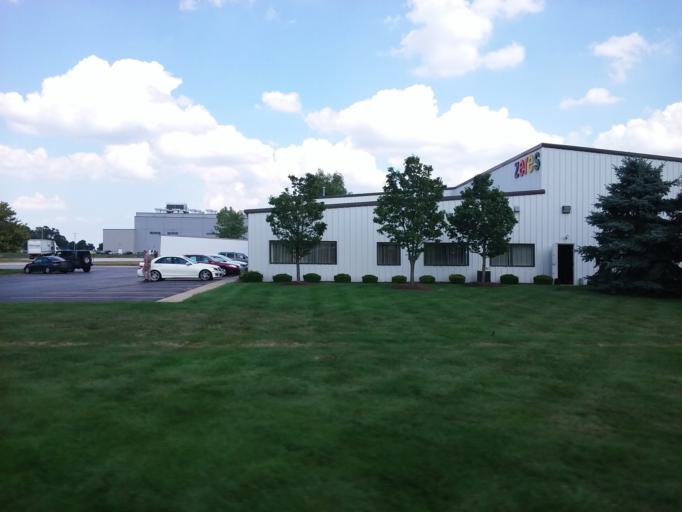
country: US
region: Ohio
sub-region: Wood County
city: Bowling Green
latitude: 41.3837
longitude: -83.6103
